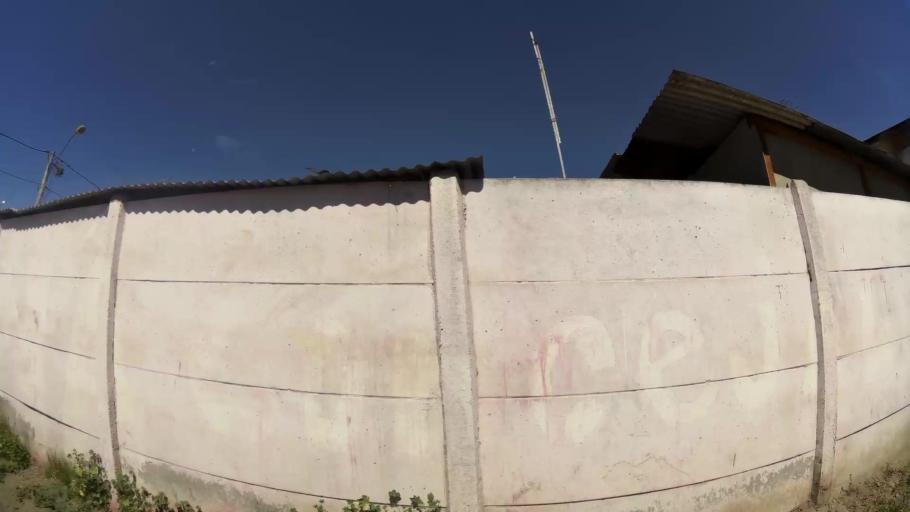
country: CL
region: Santiago Metropolitan
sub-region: Provincia de Maipo
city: San Bernardo
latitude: -33.5745
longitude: -70.6785
